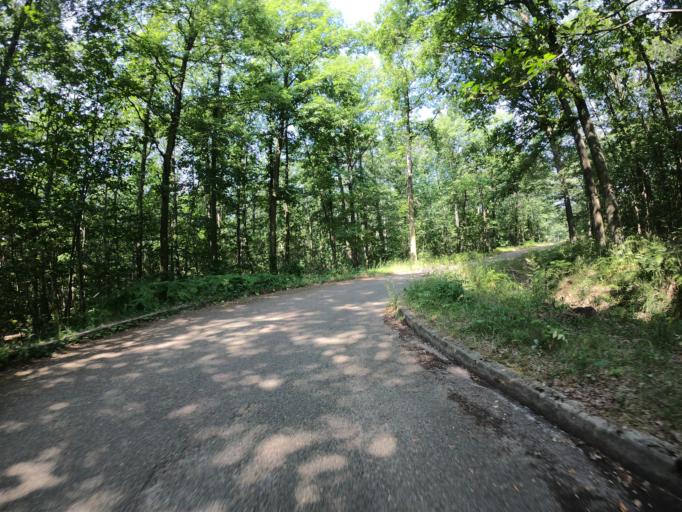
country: FR
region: Ile-de-France
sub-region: Departement de l'Essonne
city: Igny
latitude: 48.7466
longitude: 2.2404
